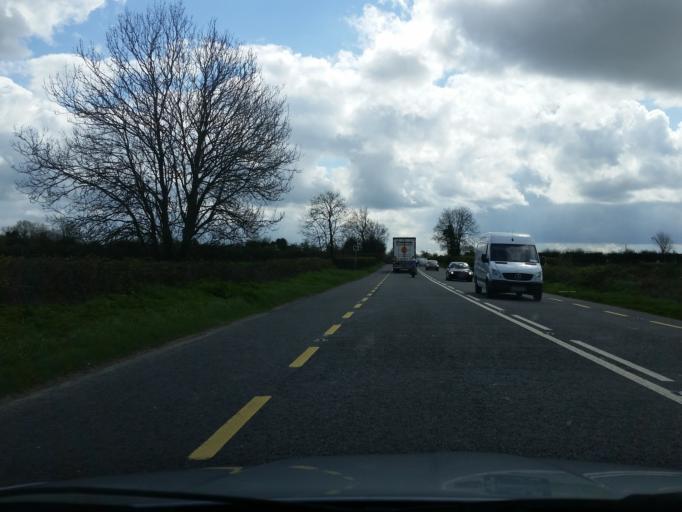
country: IE
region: Leinster
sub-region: An Mhi
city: Ratoath
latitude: 53.5674
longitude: -6.4462
